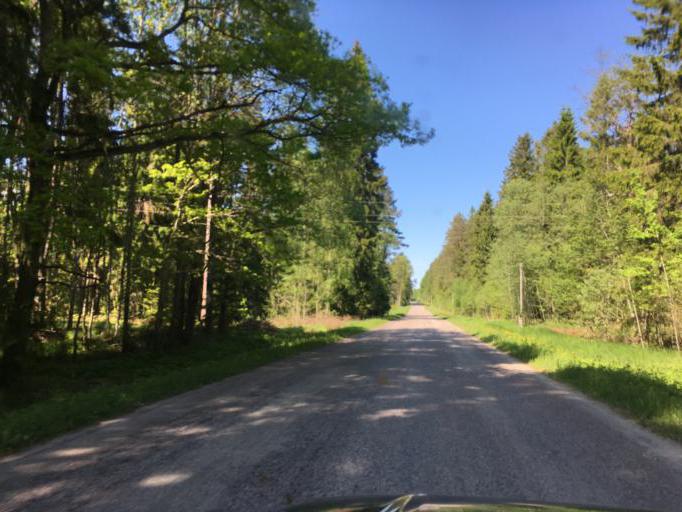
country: LV
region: Dundaga
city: Dundaga
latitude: 57.4850
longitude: 22.3405
